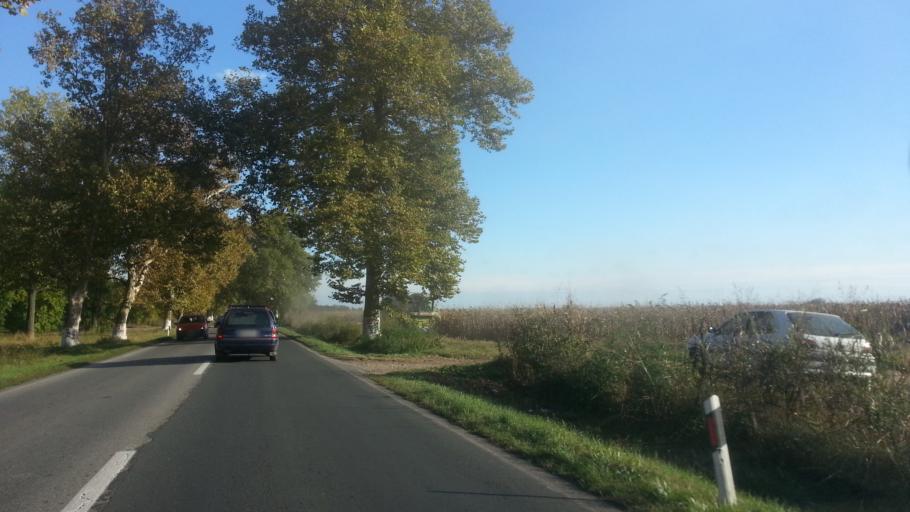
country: RS
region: Autonomna Pokrajina Vojvodina
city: Nova Pazova
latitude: 44.9301
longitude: 20.2399
